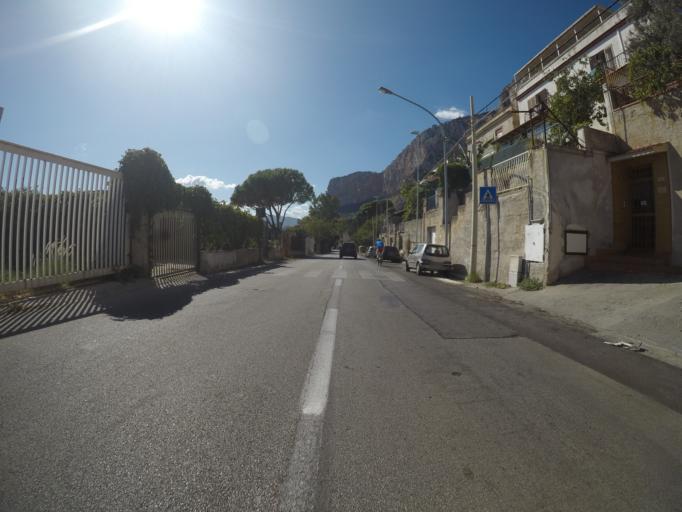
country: IT
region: Sicily
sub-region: Palermo
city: Palermo
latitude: 38.1734
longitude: 13.3661
